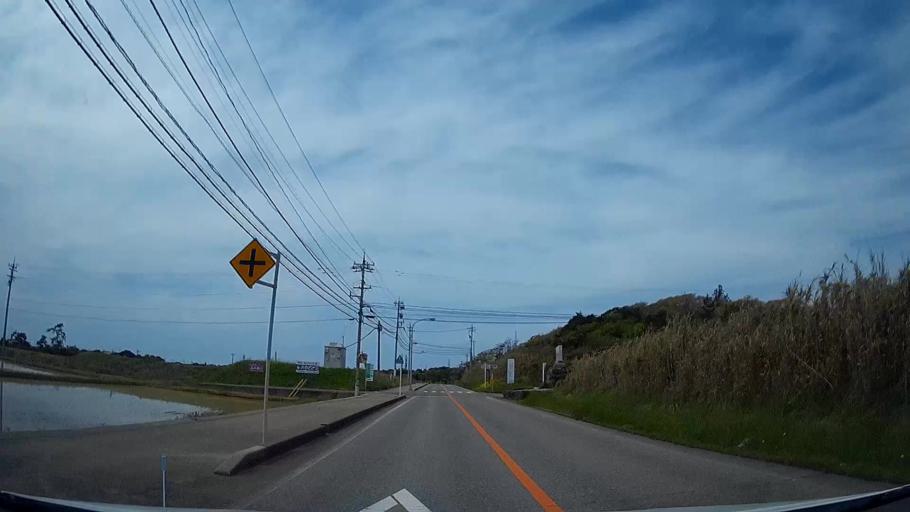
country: JP
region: Ishikawa
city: Hakui
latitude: 37.0476
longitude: 136.7372
